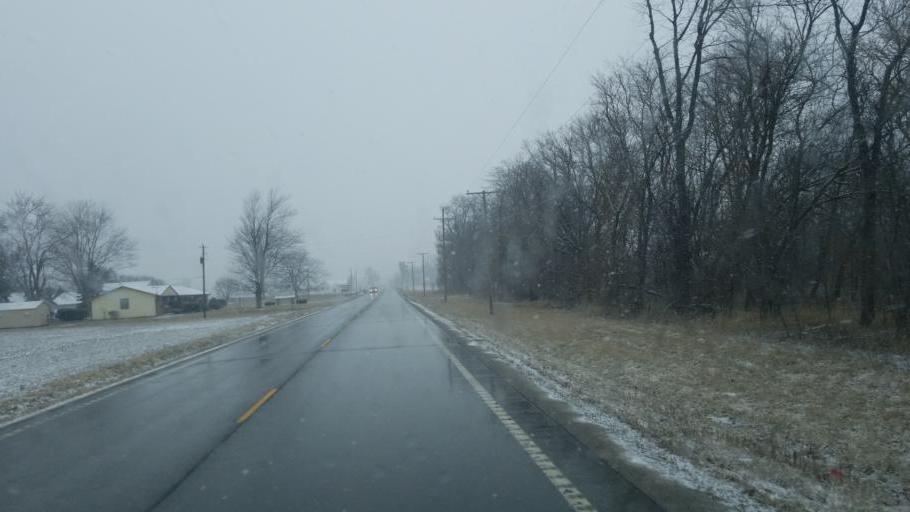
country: US
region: Ohio
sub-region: Defiance County
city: Hicksville
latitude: 41.3079
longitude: -84.7474
